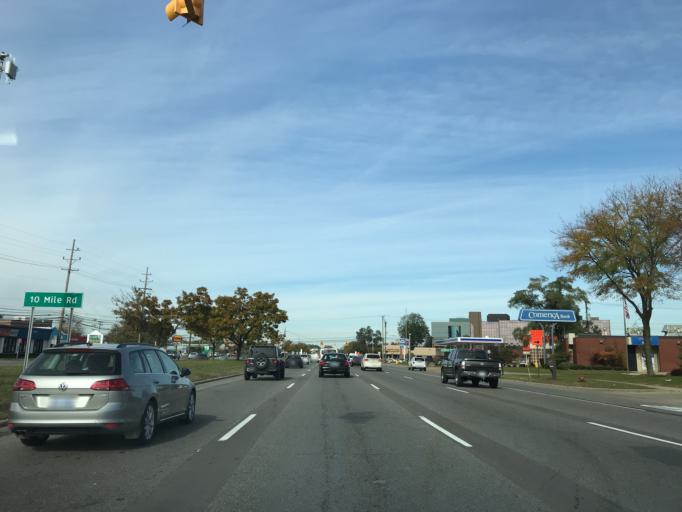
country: US
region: Michigan
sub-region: Oakland County
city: Bingham Farms
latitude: 42.4702
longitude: -83.2805
